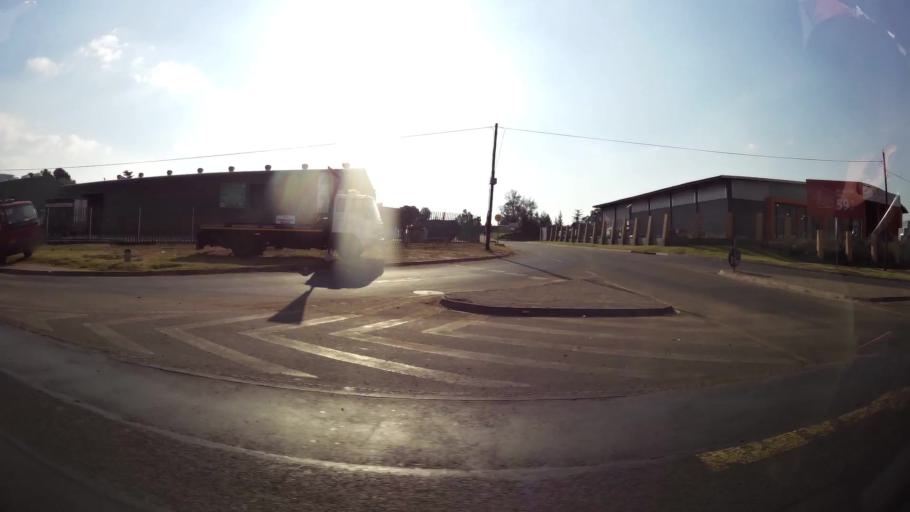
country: ZA
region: Gauteng
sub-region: City of Johannesburg Metropolitan Municipality
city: Modderfontein
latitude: -26.0945
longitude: 28.2617
